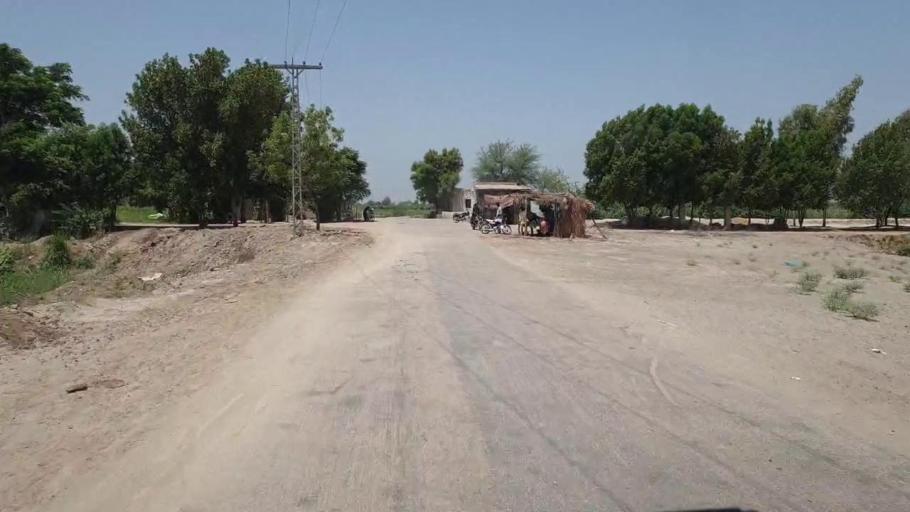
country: PK
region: Sindh
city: Nawabshah
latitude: 26.3432
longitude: 68.3828
